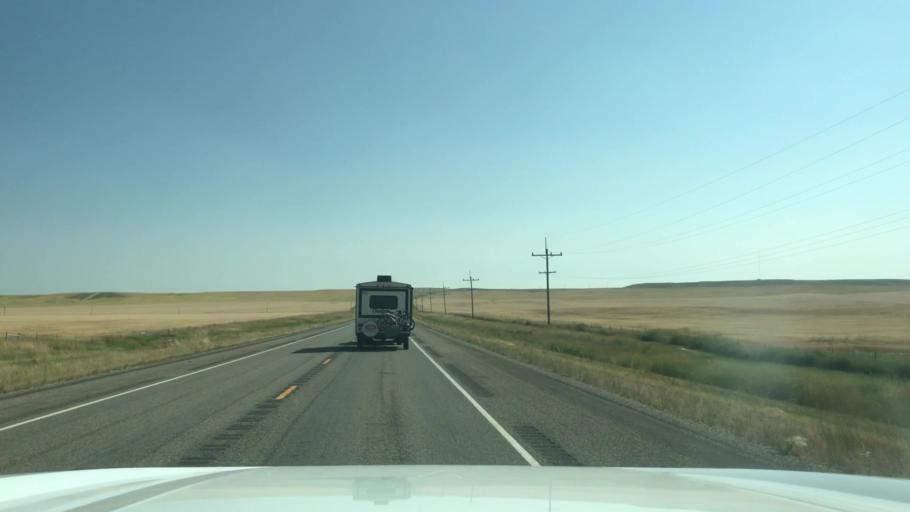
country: US
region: Montana
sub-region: Wheatland County
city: Harlowton
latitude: 46.4866
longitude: -109.7661
